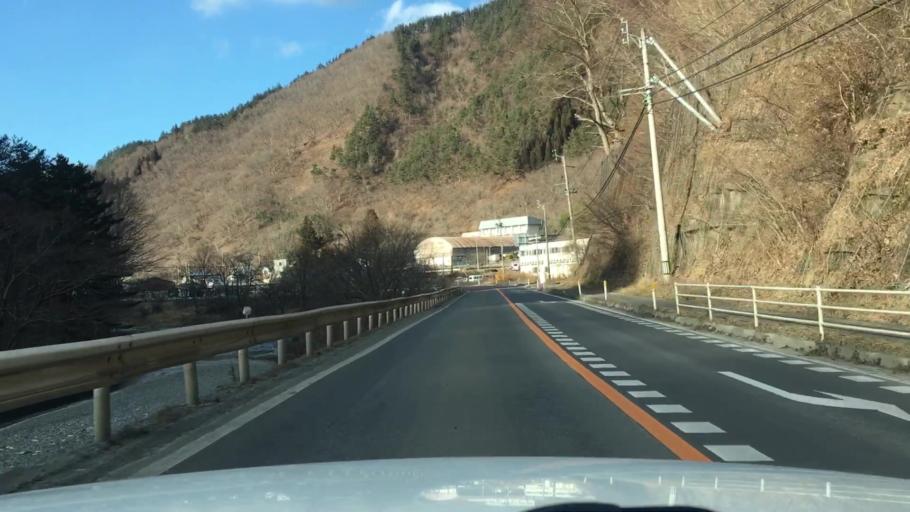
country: JP
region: Iwate
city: Miyako
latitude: 39.5910
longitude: 141.6655
